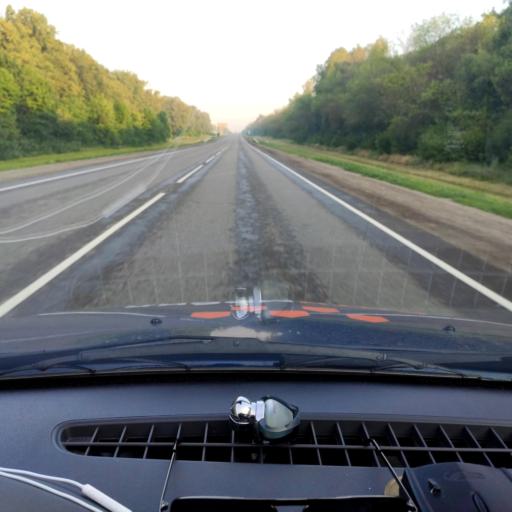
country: RU
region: Lipetsk
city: Yelets
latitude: 52.5857
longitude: 38.6169
